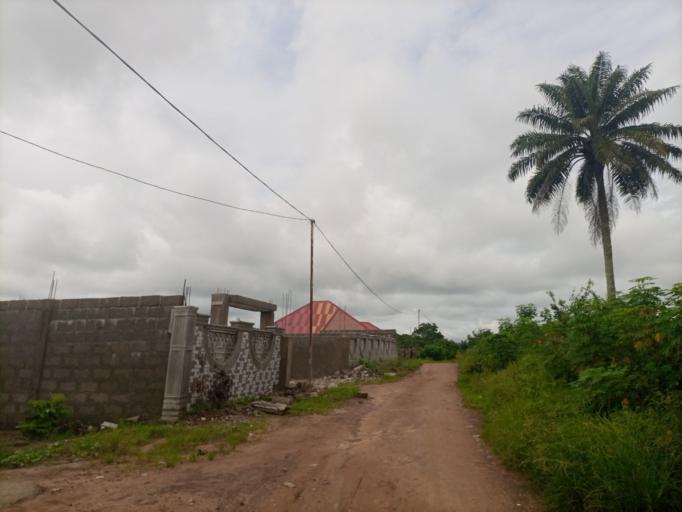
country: SL
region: Northern Province
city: Masoyila
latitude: 8.5938
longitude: -13.1761
